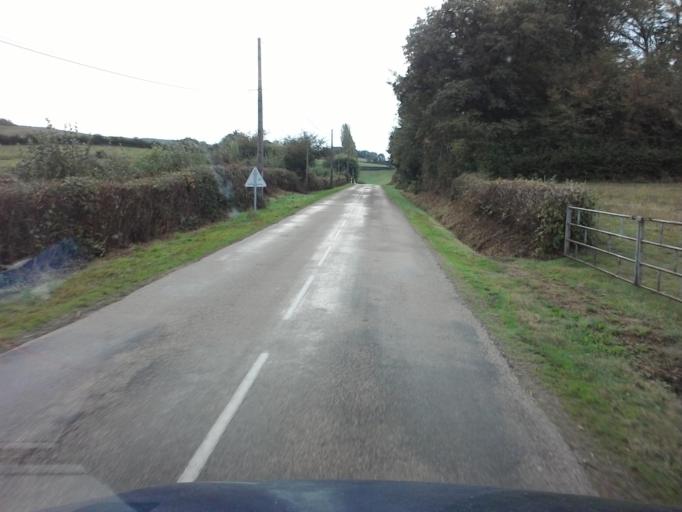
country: FR
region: Bourgogne
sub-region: Departement de la Nievre
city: Lormes
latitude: 47.1984
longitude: 3.8482
